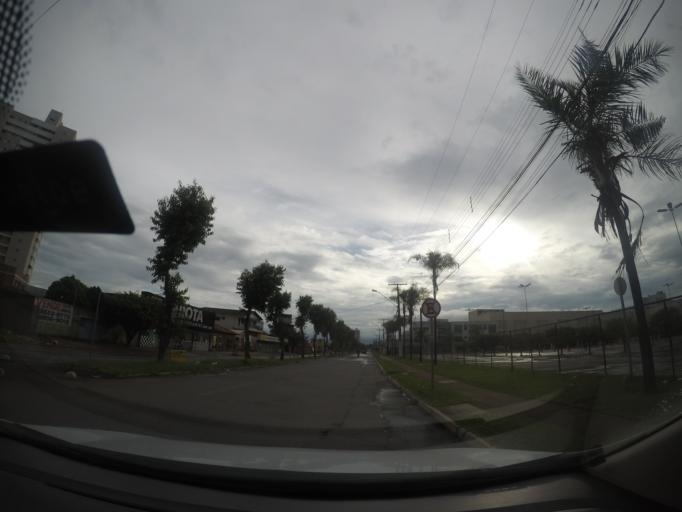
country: BR
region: Goias
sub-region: Goiania
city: Goiania
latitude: -16.7409
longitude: -49.2789
